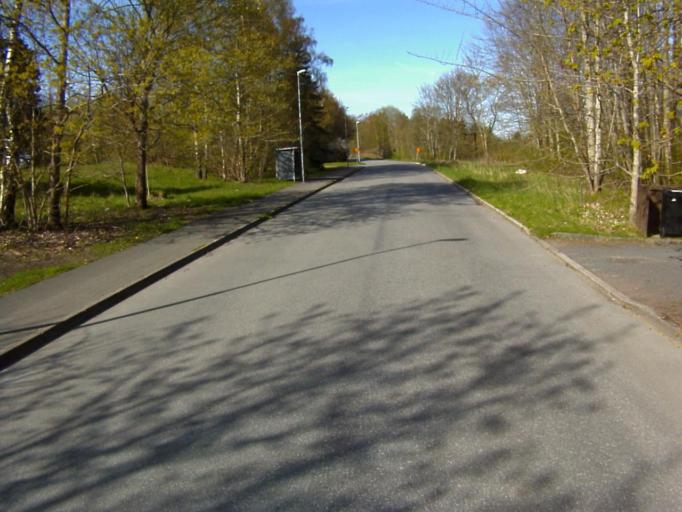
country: SE
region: Skane
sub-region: Kristianstads Kommun
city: Onnestad
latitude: 55.9944
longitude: 14.0367
